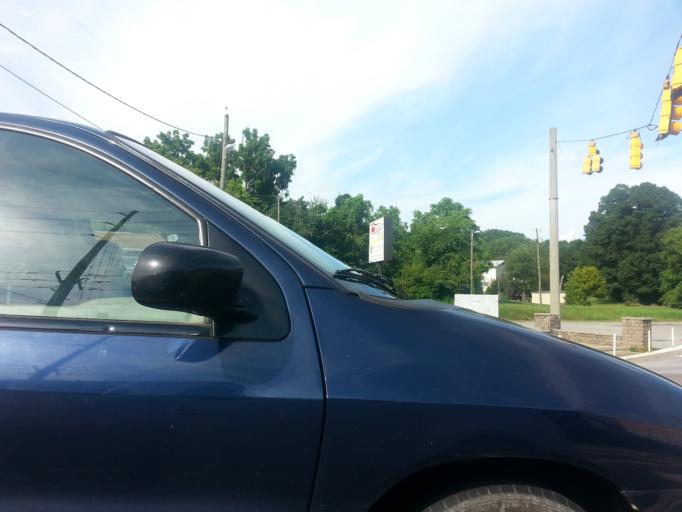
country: US
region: Tennessee
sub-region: Sevier County
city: Seymour
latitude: 35.8842
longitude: -83.7918
